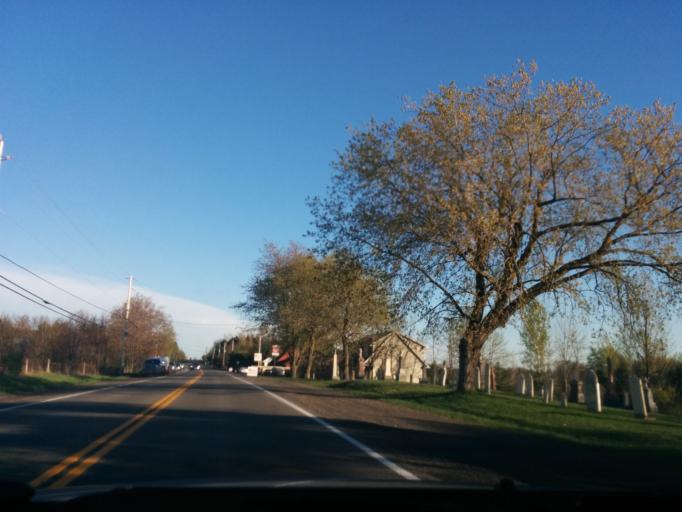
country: CA
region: Ontario
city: Ottawa
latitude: 45.1996
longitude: -75.6380
